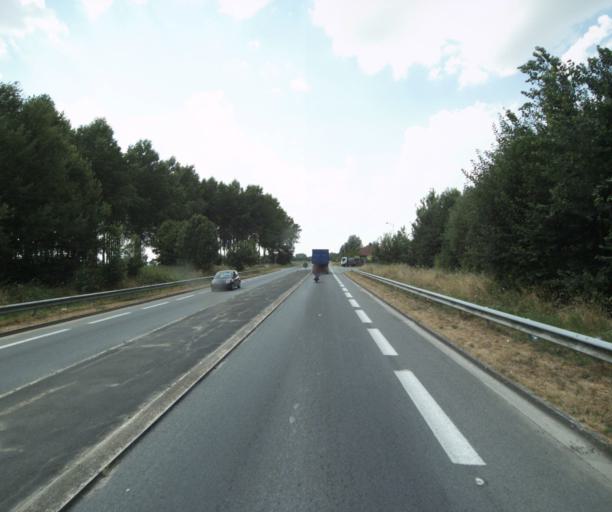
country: FR
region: Nord-Pas-de-Calais
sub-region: Departement du Nord
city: Comines
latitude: 50.7509
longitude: 2.9961
